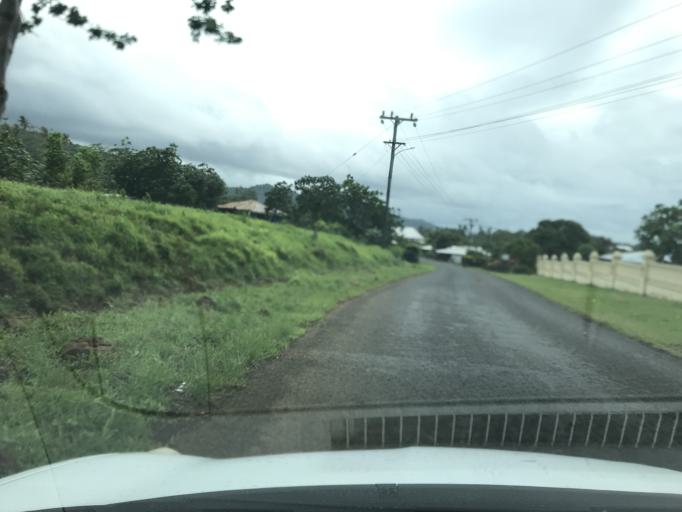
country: WS
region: Atua
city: Lufilufi
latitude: -13.8758
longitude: -171.5998
